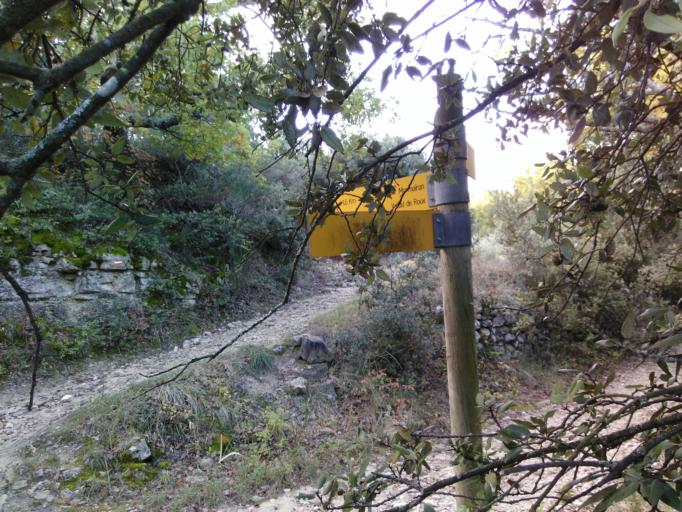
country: FR
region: Provence-Alpes-Cote d'Azur
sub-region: Departement du Vaucluse
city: Mormoiron
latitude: 44.0749
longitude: 5.1683
